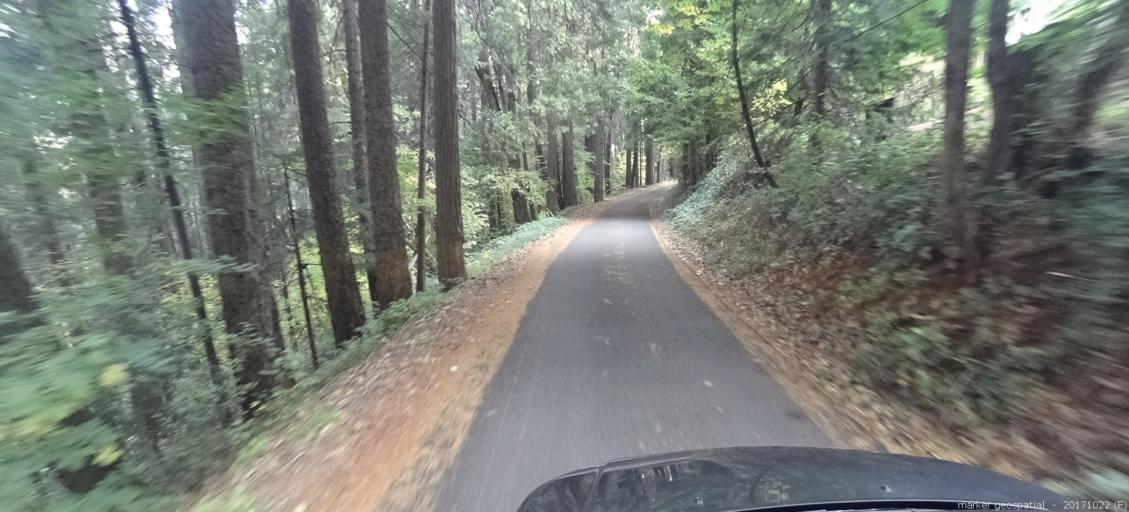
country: US
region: California
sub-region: Siskiyou County
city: Dunsmuir
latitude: 41.1553
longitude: -122.2894
